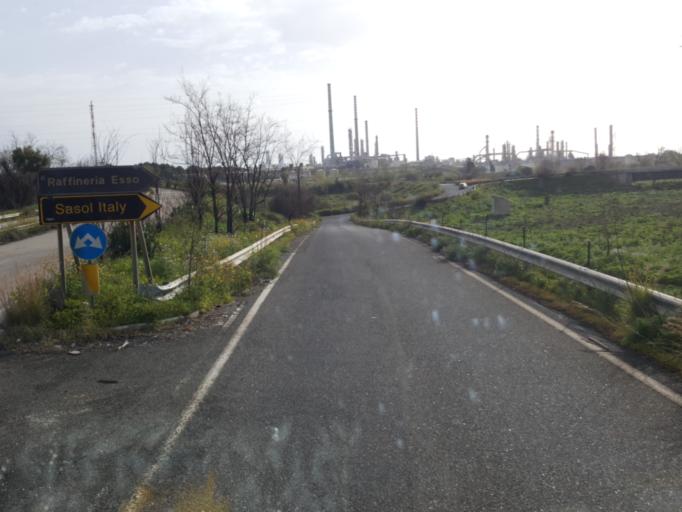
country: IT
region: Sicily
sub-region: Provincia di Siracusa
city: Melilli
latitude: 37.2200
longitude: 15.1628
